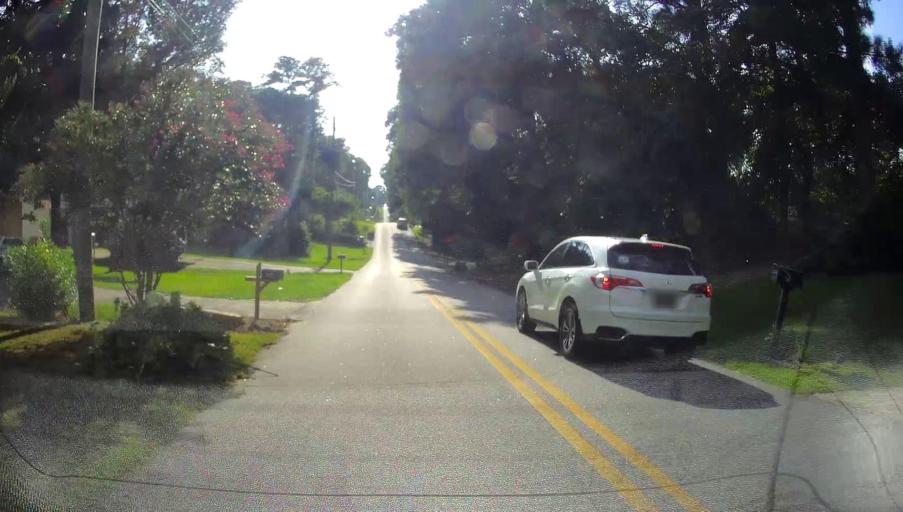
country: US
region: Georgia
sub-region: Houston County
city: Warner Robins
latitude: 32.5994
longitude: -83.6467
